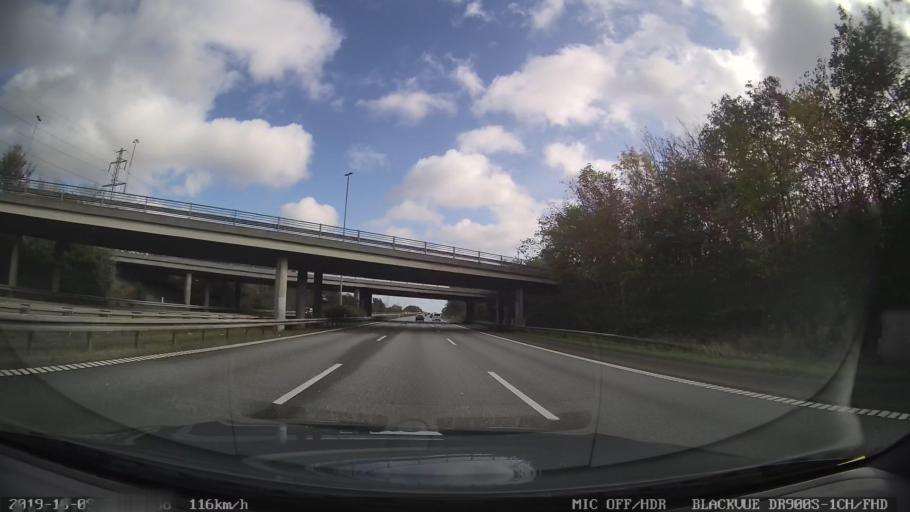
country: DK
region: Capital Region
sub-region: Vallensbaek Kommune
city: Vallensbaek
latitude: 55.6278
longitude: 12.3820
